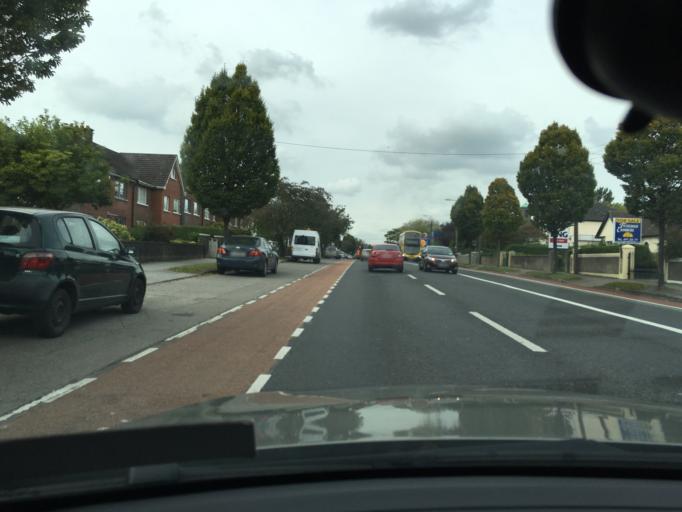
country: IE
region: Leinster
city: Cabra
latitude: 53.3656
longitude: -6.3105
